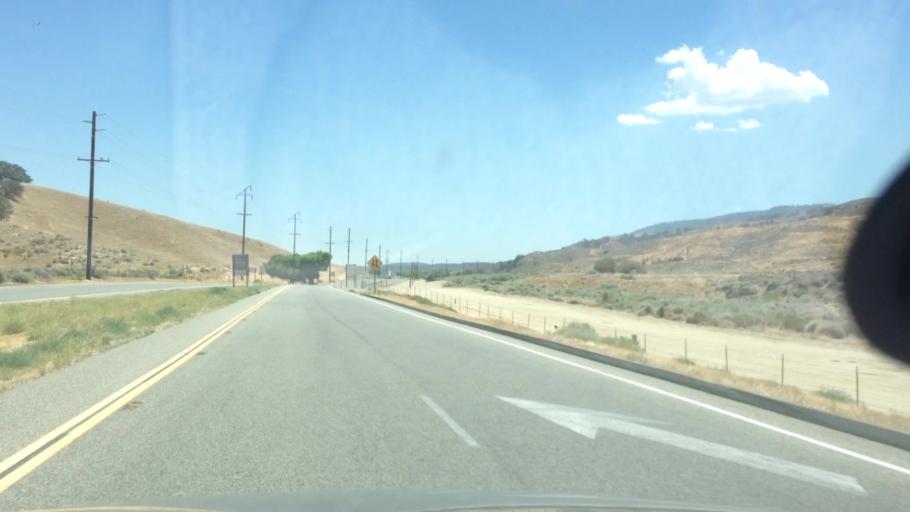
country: US
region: California
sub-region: Kern County
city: Lebec
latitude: 34.7742
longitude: -118.7687
